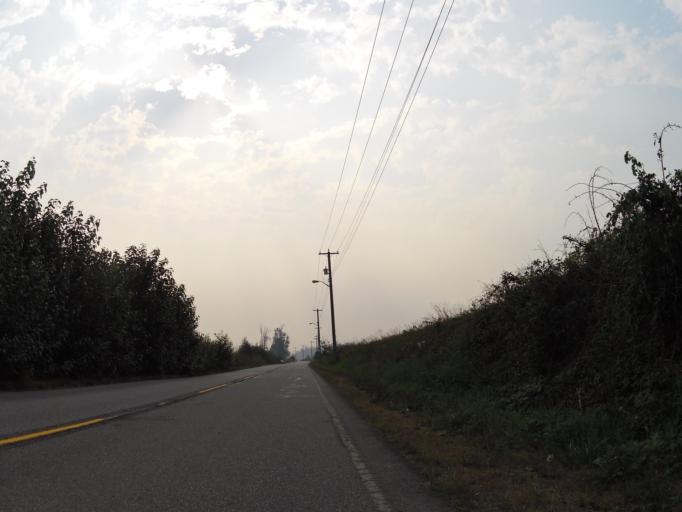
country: CA
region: British Columbia
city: Burnaby
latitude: 49.1898
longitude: -123.0024
